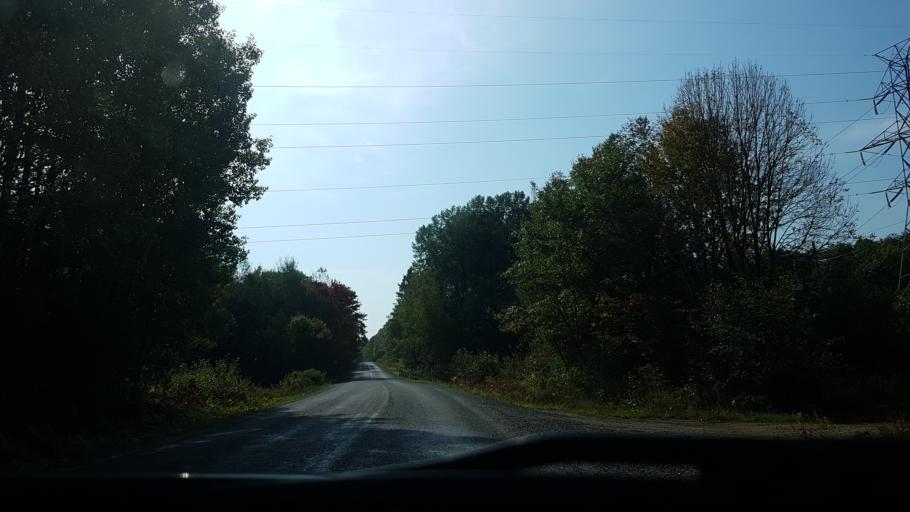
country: CA
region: Ontario
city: Gravenhurst
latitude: 44.8052
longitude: -79.2106
